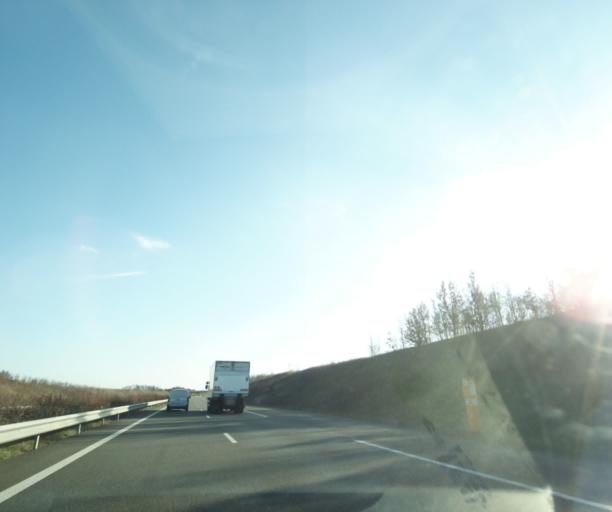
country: FR
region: Midi-Pyrenees
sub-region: Departement du Tarn-et-Garonne
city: Caussade
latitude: 44.2241
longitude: 1.5365
